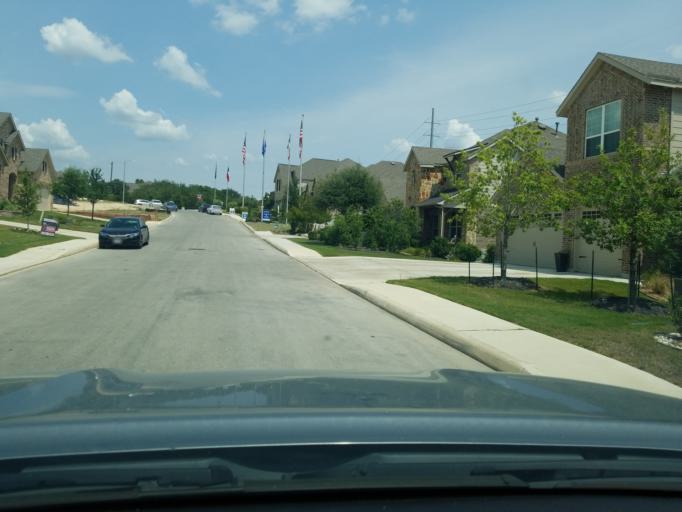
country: US
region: Texas
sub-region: Bexar County
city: Timberwood Park
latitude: 29.6802
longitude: -98.4792
